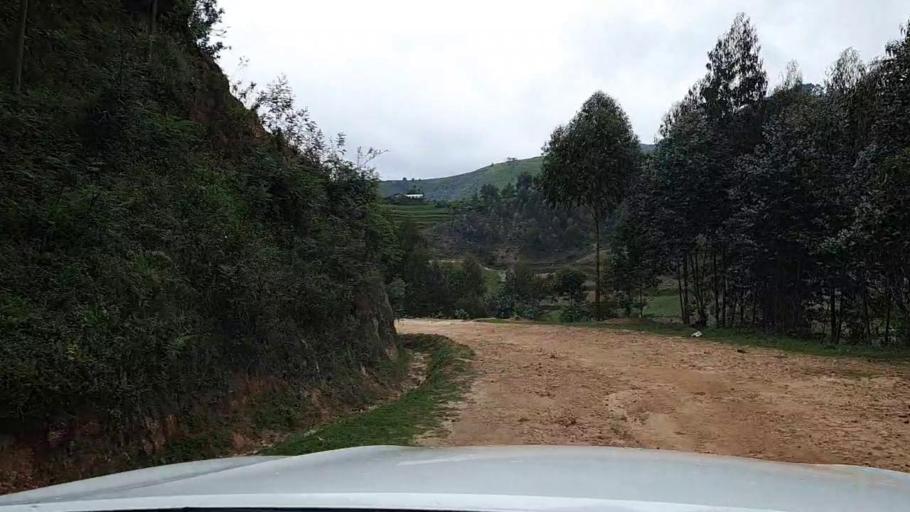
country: RW
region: Western Province
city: Kibuye
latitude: -2.2872
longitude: 29.3689
